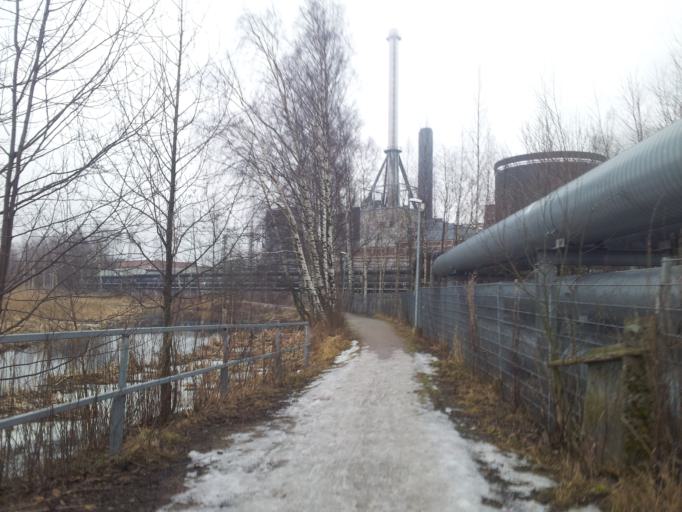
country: FI
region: Uusimaa
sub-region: Helsinki
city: Koukkuniemi
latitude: 60.1511
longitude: 24.7151
